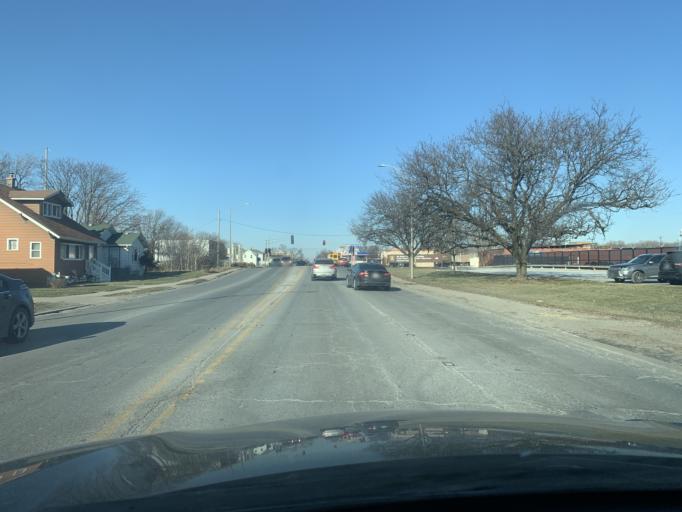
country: US
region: Illinois
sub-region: Cook County
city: Maywood
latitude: 41.8745
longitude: -87.8338
